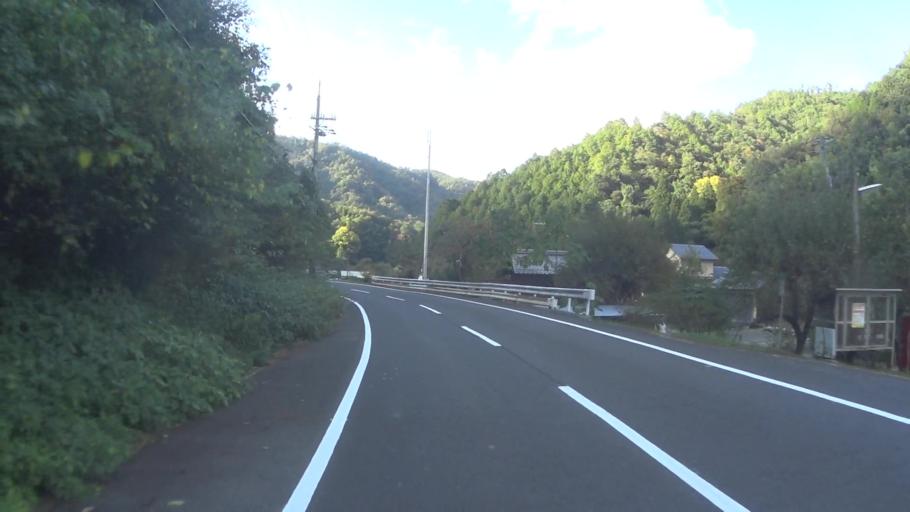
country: JP
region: Kyoto
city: Maizuru
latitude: 35.4612
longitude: 135.2587
